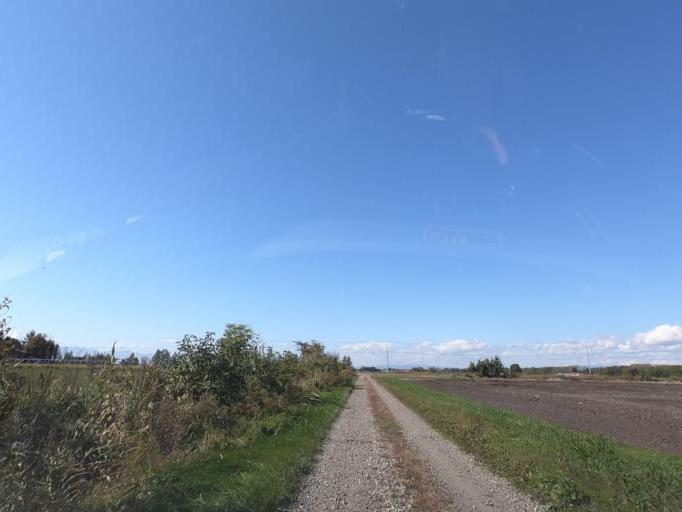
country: JP
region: Hokkaido
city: Otofuke
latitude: 43.0715
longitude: 143.2603
